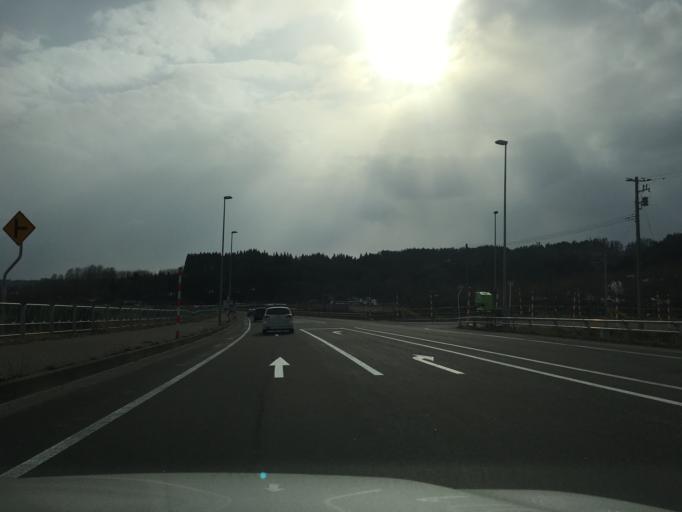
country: JP
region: Aomori
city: Namioka
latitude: 40.7670
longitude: 140.5905
